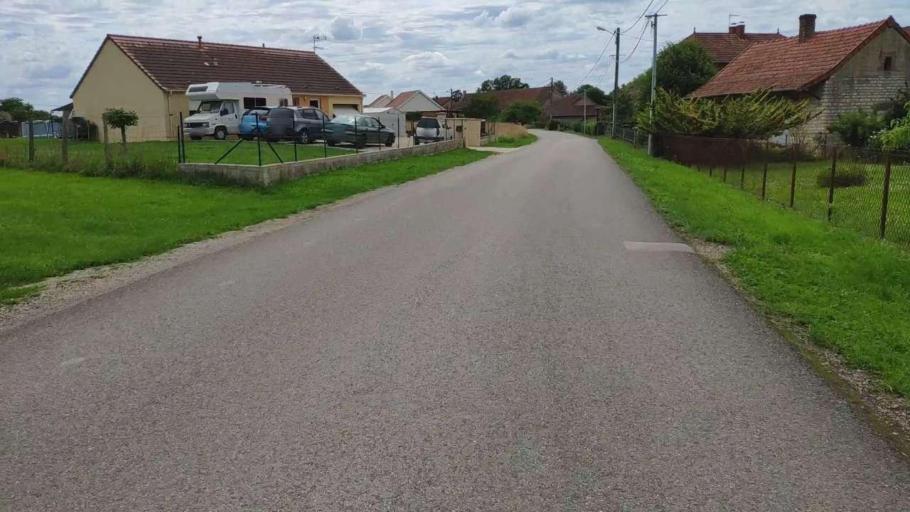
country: FR
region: Franche-Comte
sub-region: Departement du Jura
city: Chaussin
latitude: 46.8734
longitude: 5.4328
